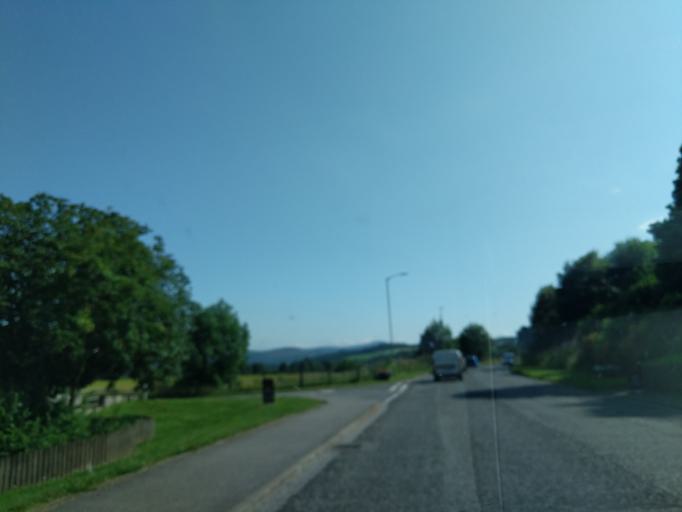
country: GB
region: Scotland
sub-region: Moray
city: Rothes
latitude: 57.5229
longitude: -3.2086
